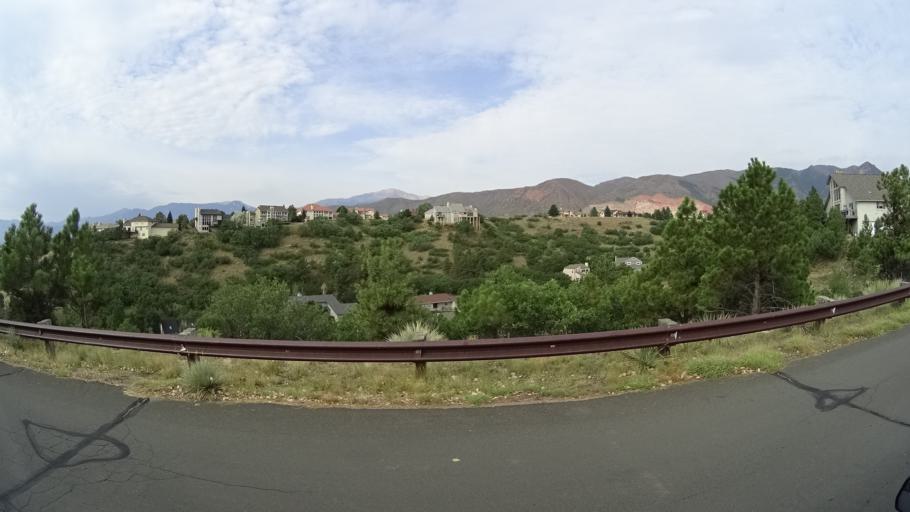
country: US
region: Colorado
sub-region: El Paso County
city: Air Force Academy
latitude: 38.9332
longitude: -104.8568
